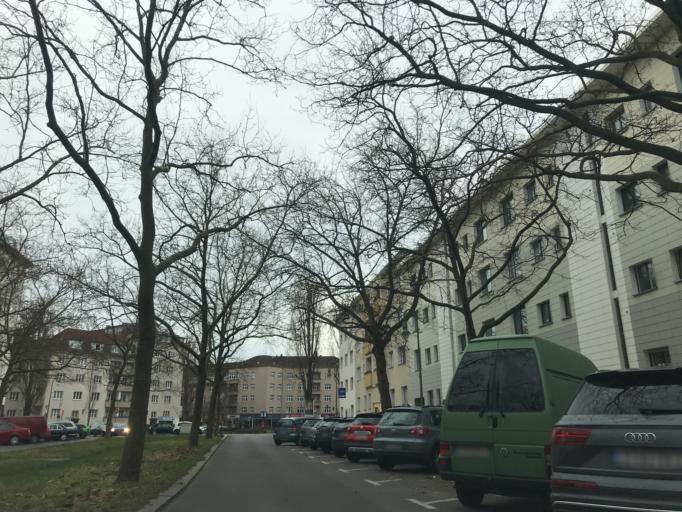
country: DE
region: Berlin
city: Westend
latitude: 52.5177
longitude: 13.2612
